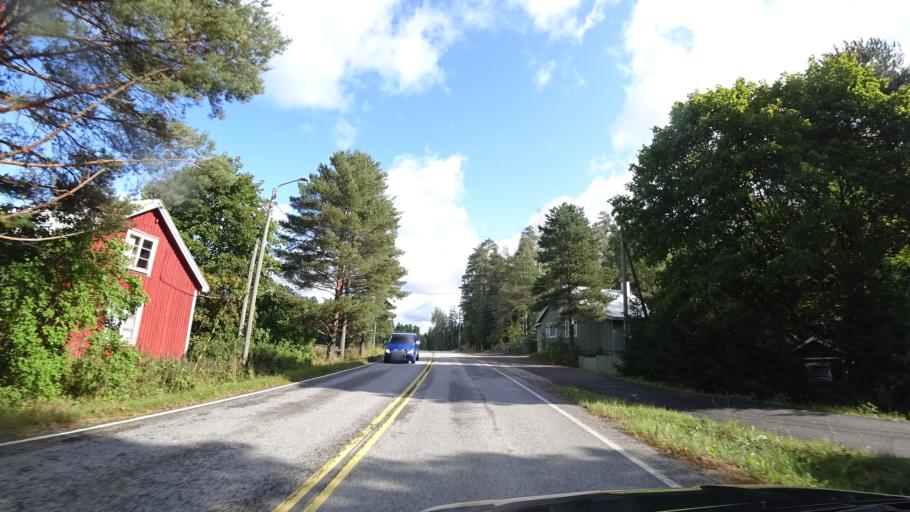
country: FI
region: Uusimaa
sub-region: Helsinki
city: Jaervenpaeae
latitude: 60.5833
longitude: 25.0042
